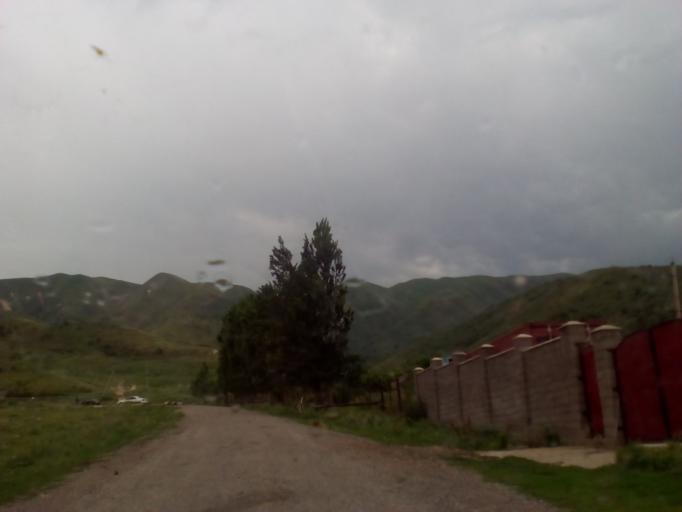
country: KZ
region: Almaty Oblysy
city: Burunday
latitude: 43.1514
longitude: 76.3852
